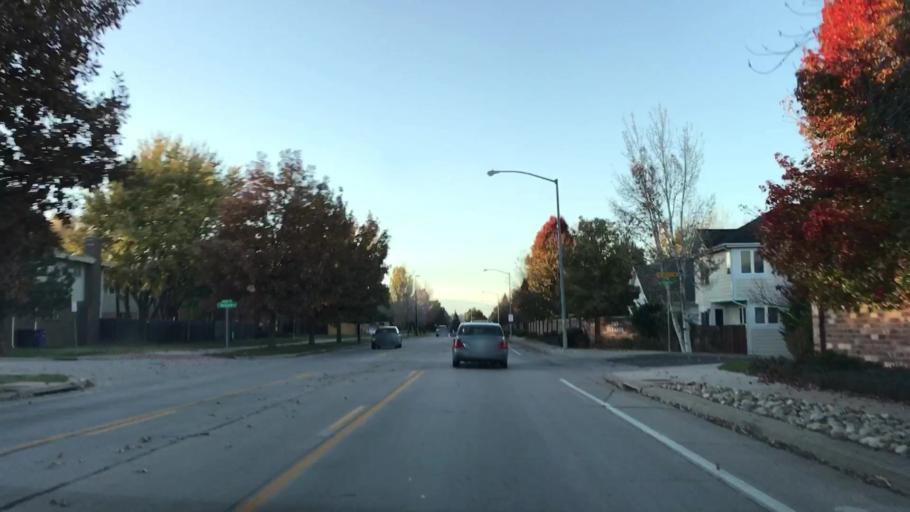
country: US
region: Colorado
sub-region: Arapahoe County
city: Glendale
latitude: 39.6647
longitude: -104.8906
